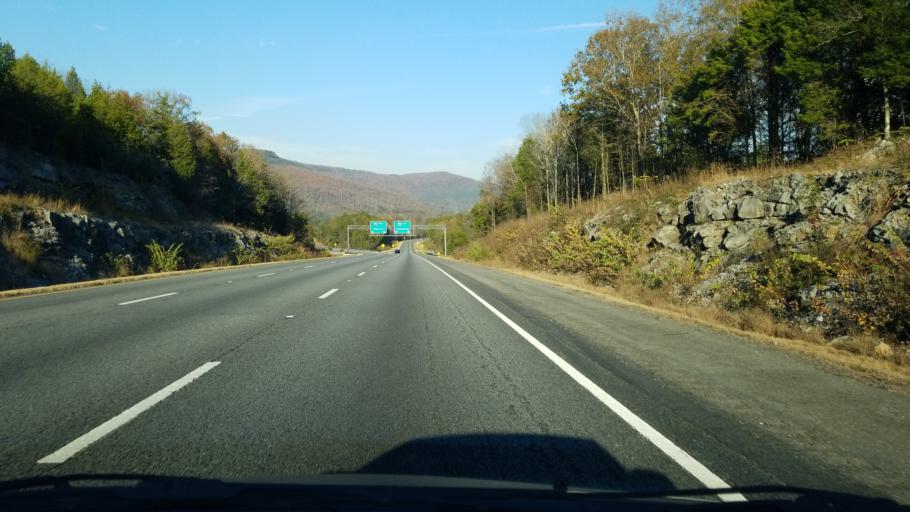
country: US
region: Georgia
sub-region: Walker County
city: Lookout Mountain
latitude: 34.9639
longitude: -85.4544
